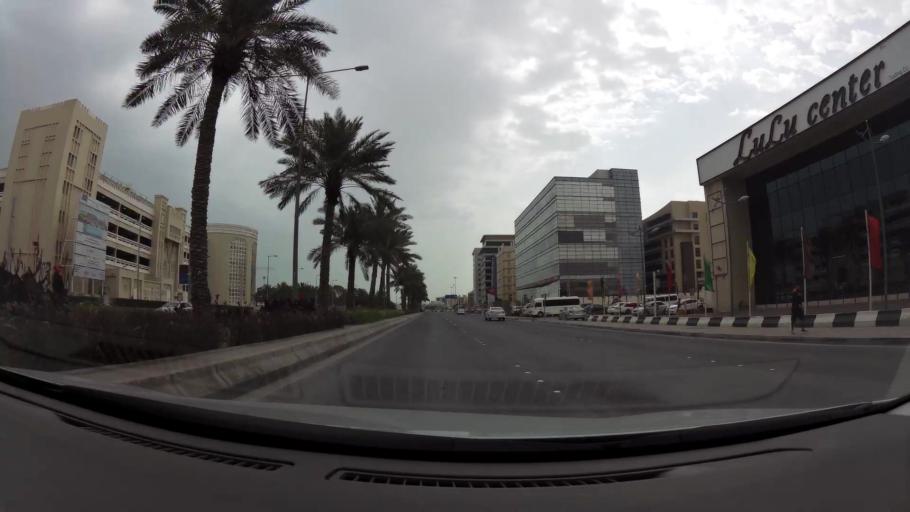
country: QA
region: Baladiyat ad Dawhah
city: Doha
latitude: 25.2912
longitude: 51.5027
